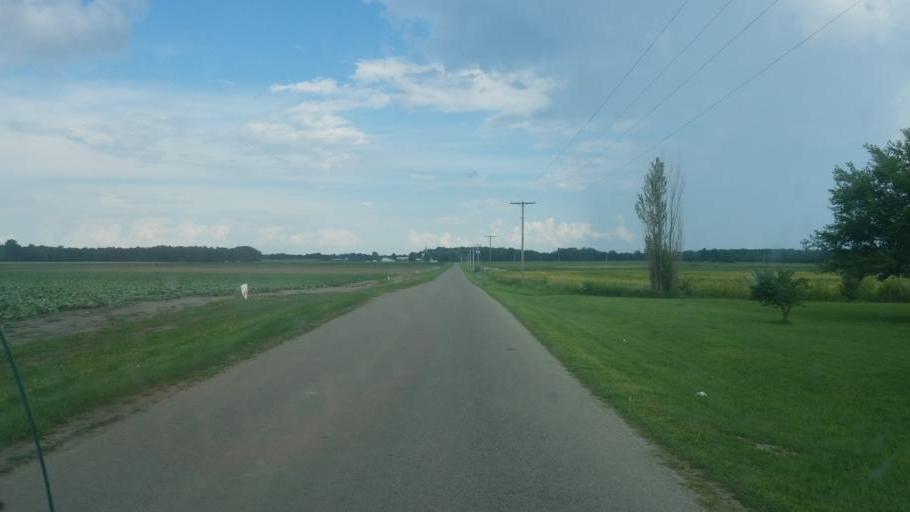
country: US
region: Ohio
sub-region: Huron County
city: Willard
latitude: 41.0186
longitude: -82.7035
